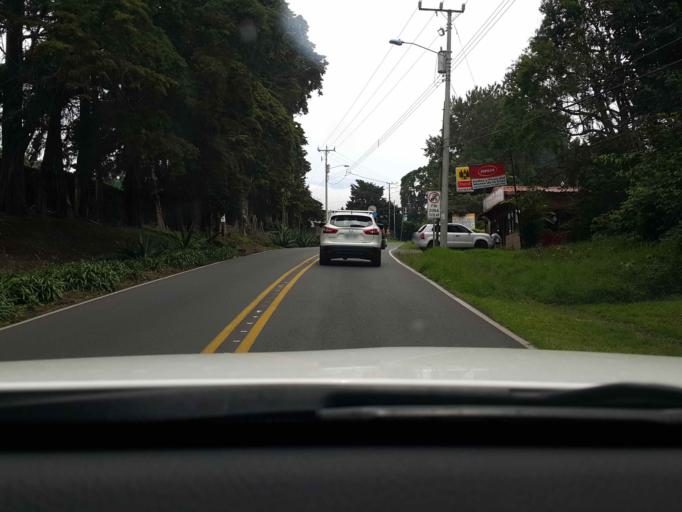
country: CR
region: Heredia
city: San Josecito
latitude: 10.0384
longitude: -84.0899
